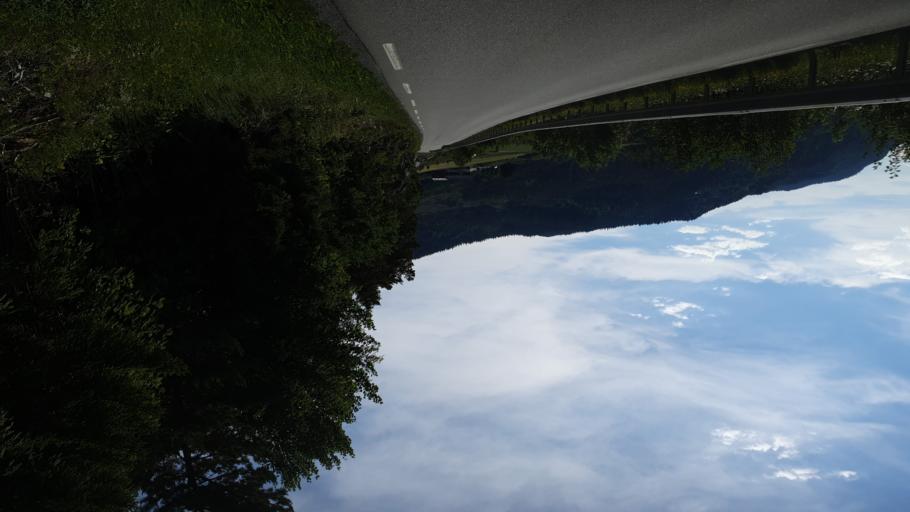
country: NO
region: Nord-Trondelag
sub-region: Leksvik
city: Leksvik
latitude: 63.6259
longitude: 10.5512
